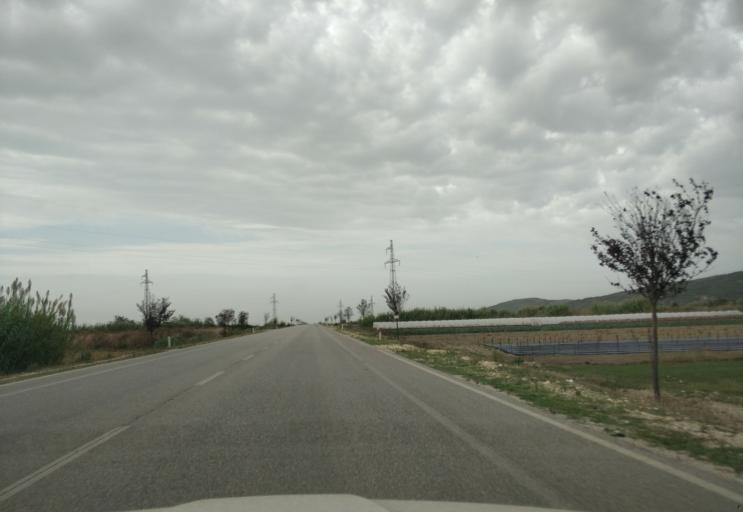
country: AL
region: Fier
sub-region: Rrethi i Fierit
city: Frakulla e Madhe
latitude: 40.6378
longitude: 19.5035
